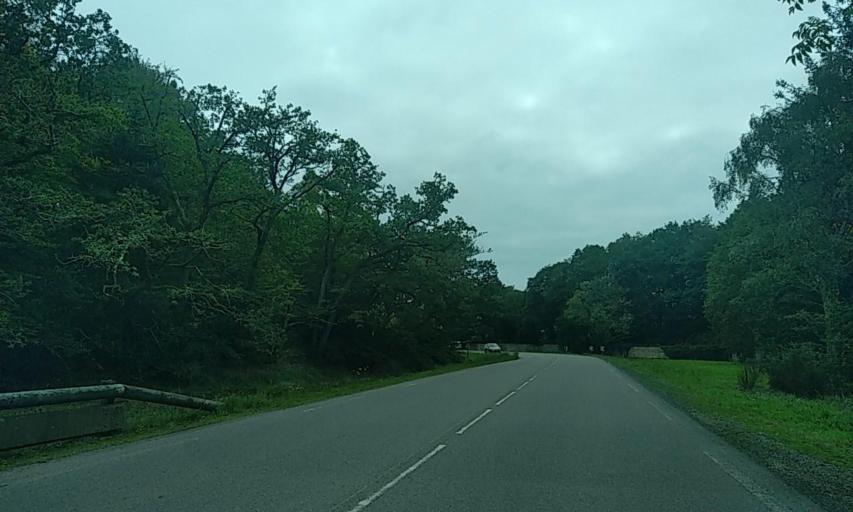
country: FR
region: Brittany
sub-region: Departement du Morbihan
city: Lorient
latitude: 47.7730
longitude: -3.3606
